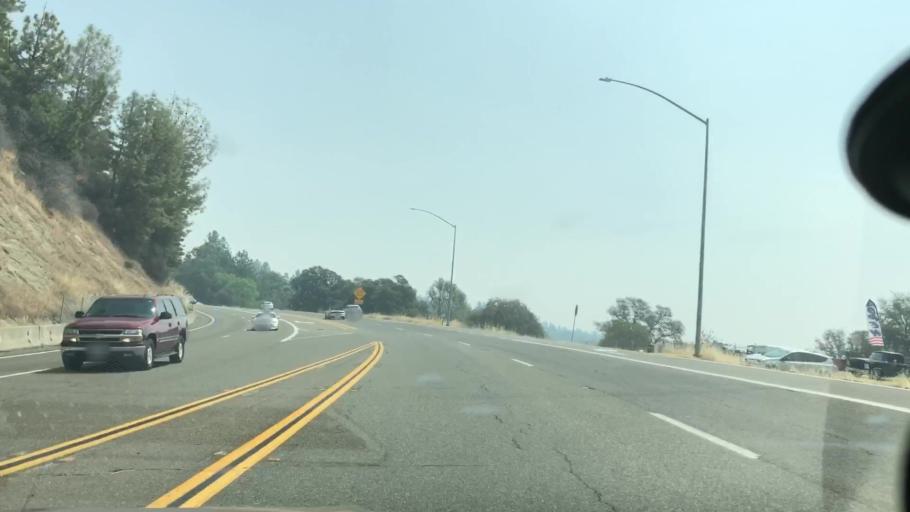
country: US
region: California
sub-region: El Dorado County
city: Camino
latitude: 38.7378
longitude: -120.7329
